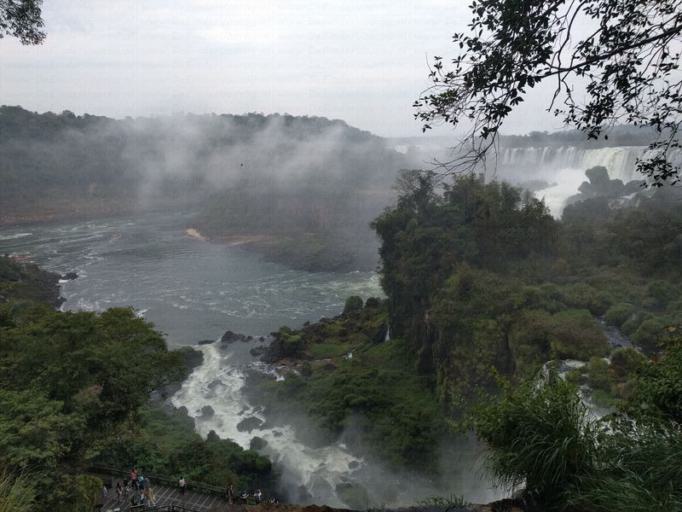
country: AR
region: Misiones
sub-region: Departamento de Iguazu
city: Puerto Iguazu
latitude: -25.6854
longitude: -54.4462
